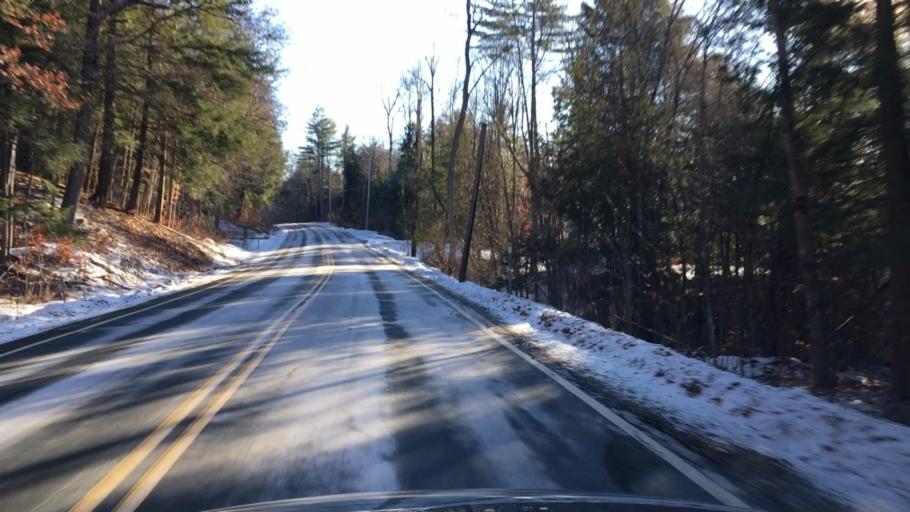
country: US
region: New Hampshire
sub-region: Grafton County
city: Woodsville
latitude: 44.2163
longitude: -72.0496
